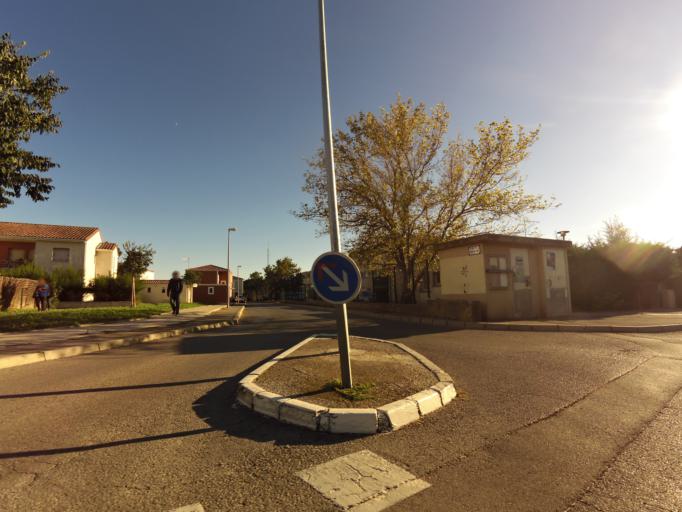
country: FR
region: Languedoc-Roussillon
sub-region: Departement de l'Herault
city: Lunel
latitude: 43.6661
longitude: 4.1321
